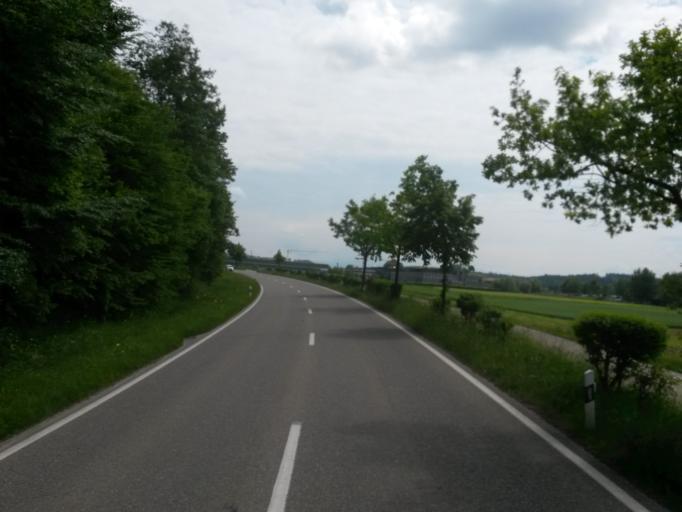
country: CH
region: Zurich
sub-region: Bezirk Pfaeffikon
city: Illnau / Unter-Illnau
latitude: 47.3992
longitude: 8.7333
